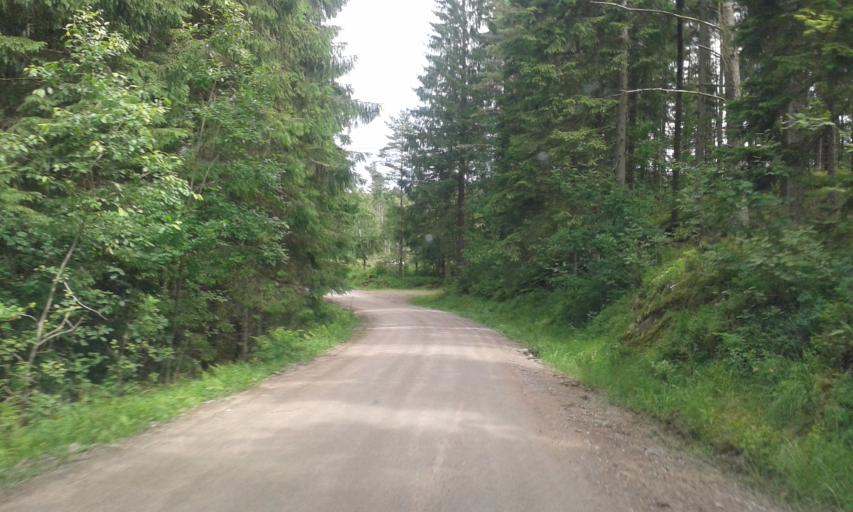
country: SE
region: Vaestra Goetaland
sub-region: Kungalvs Kommun
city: Diserod
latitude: 57.9886
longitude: 12.0207
